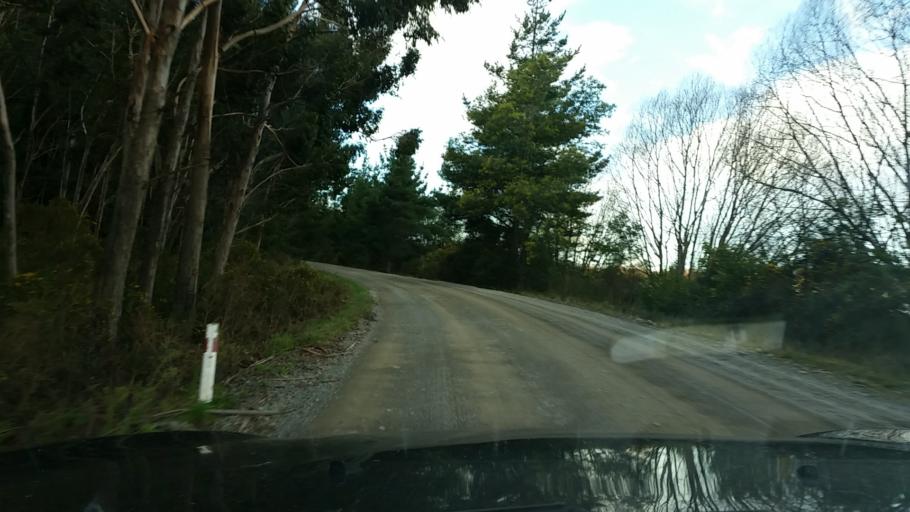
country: NZ
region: Nelson
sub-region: Nelson City
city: Nelson
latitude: -41.5742
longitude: 173.4448
